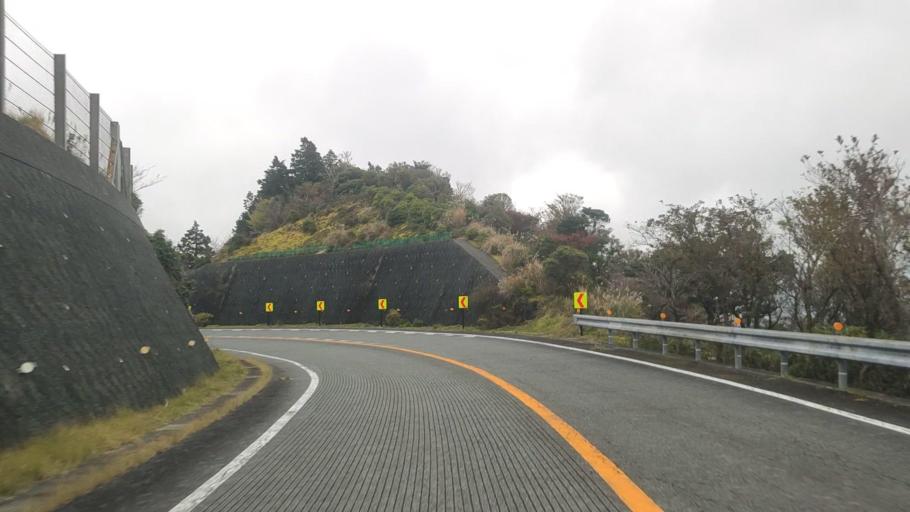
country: JP
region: Shizuoka
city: Heda
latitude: 34.8815
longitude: 138.8436
